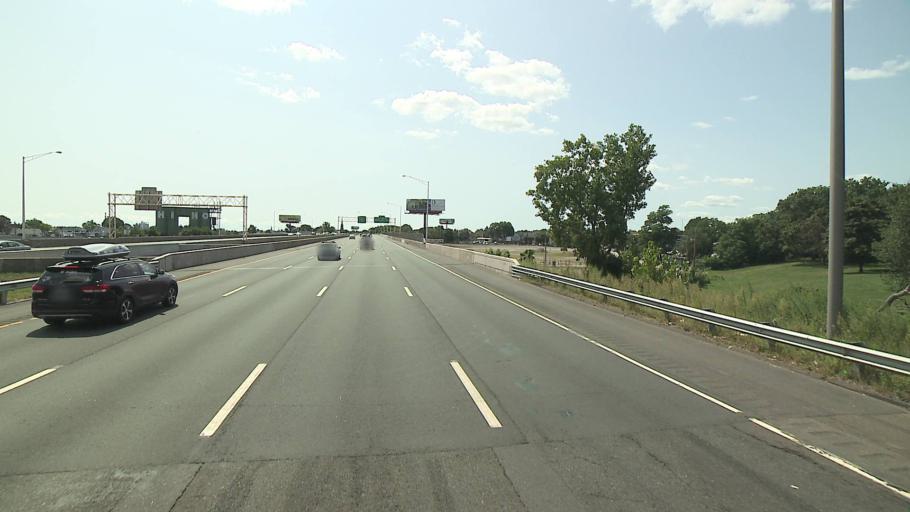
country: US
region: Connecticut
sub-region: Fairfield County
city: Bridgeport
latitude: 41.2011
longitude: -73.1934
